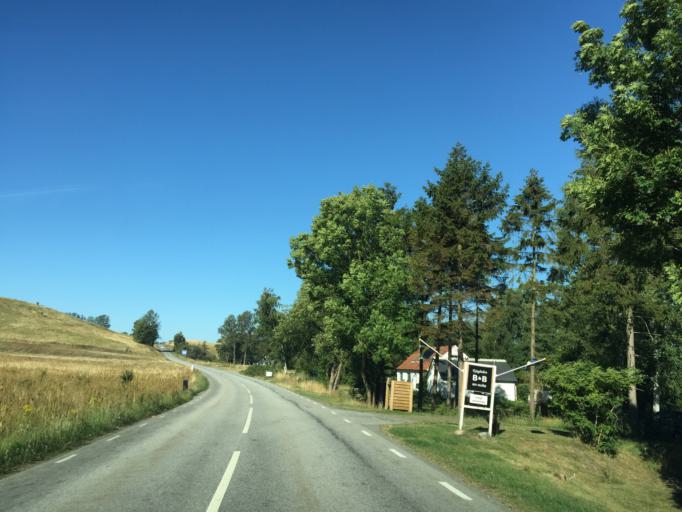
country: SE
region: Skane
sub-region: Ystads Kommun
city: Kopingebro
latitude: 55.3908
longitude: 14.0765
